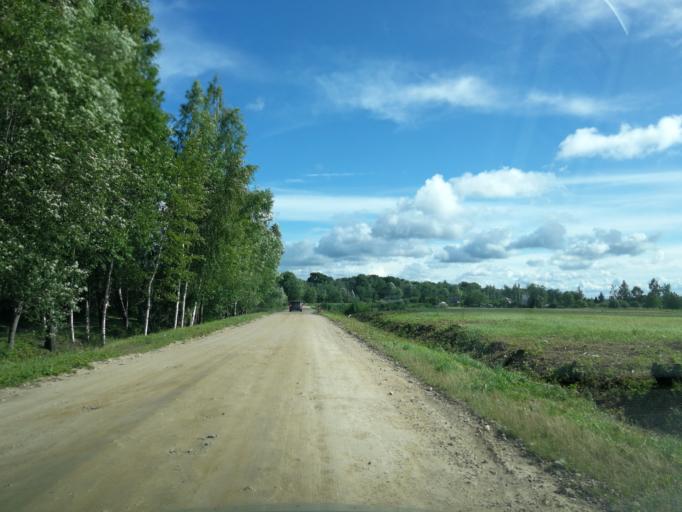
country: LV
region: Adazi
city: Adazi
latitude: 57.0971
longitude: 24.3237
